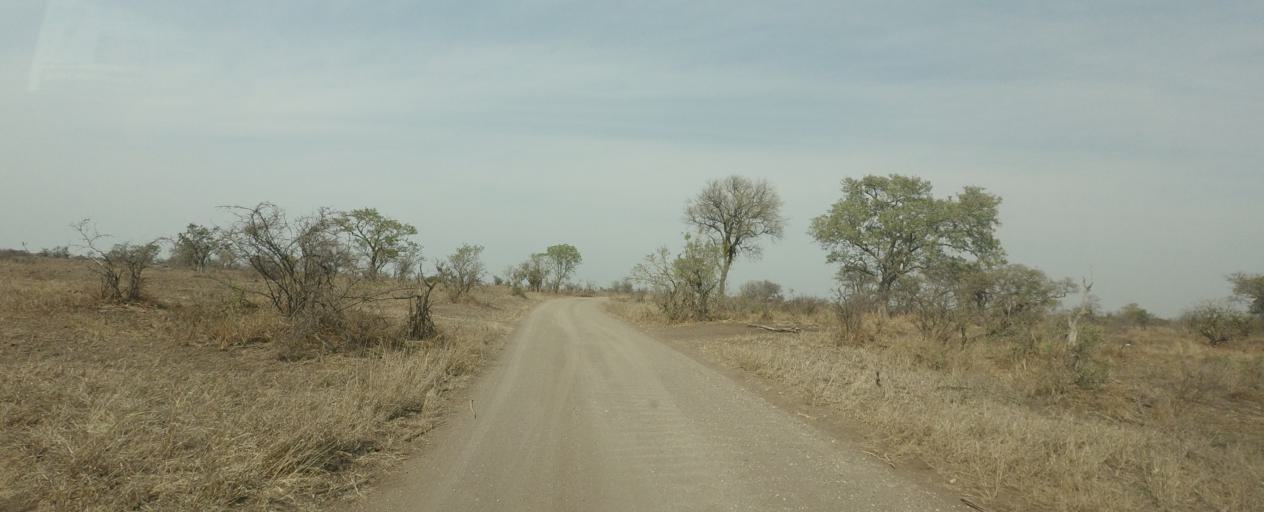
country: ZA
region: Limpopo
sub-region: Mopani District Municipality
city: Phalaborwa
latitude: -24.2608
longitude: 31.7259
